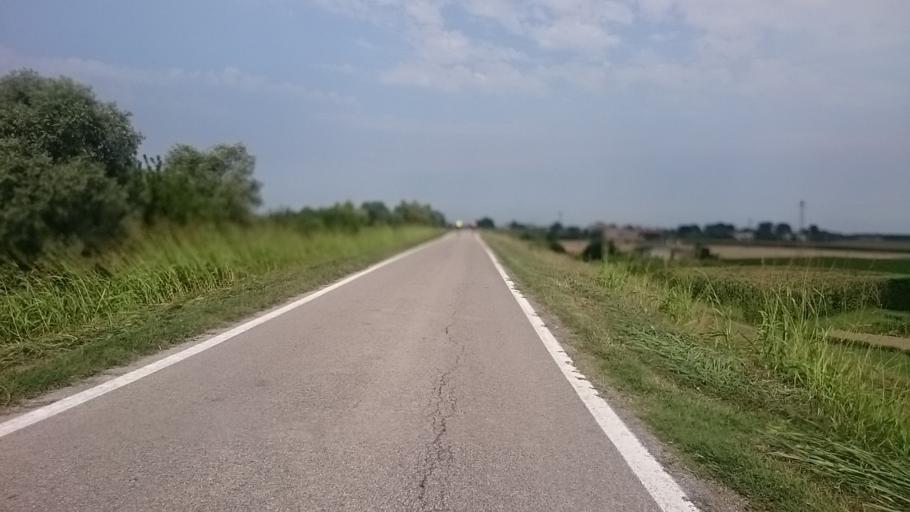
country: IT
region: Veneto
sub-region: Provincia di Padova
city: Bovolenta
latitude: 45.2730
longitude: 11.9387
